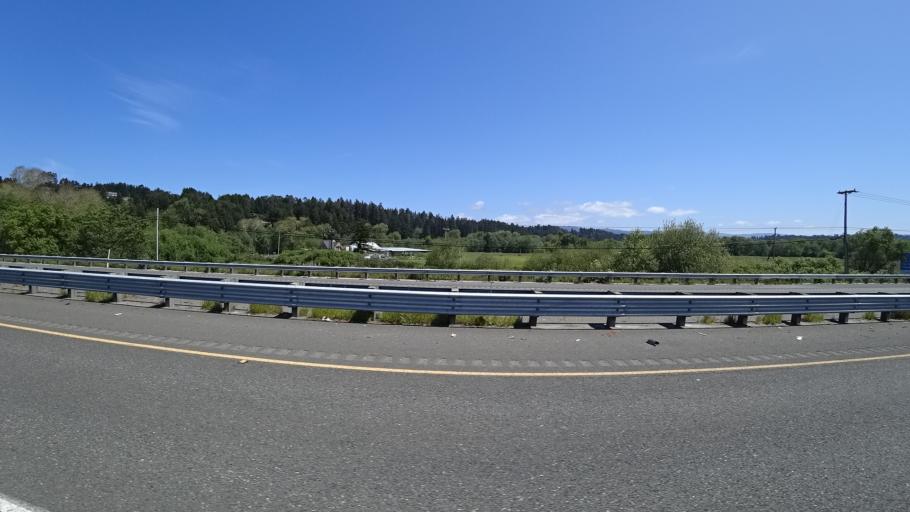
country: US
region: California
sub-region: Humboldt County
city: McKinleyville
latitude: 40.9149
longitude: -124.0923
